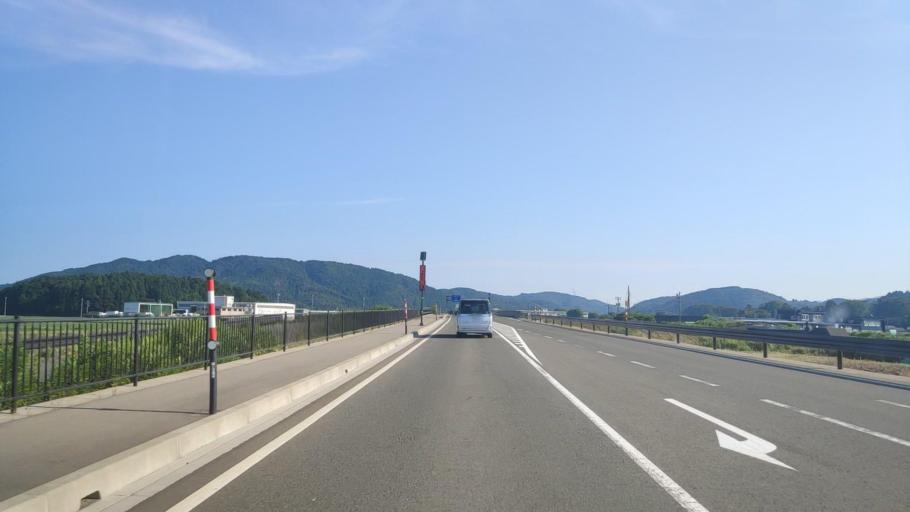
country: JP
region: Fukui
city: Maruoka
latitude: 36.1906
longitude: 136.2682
